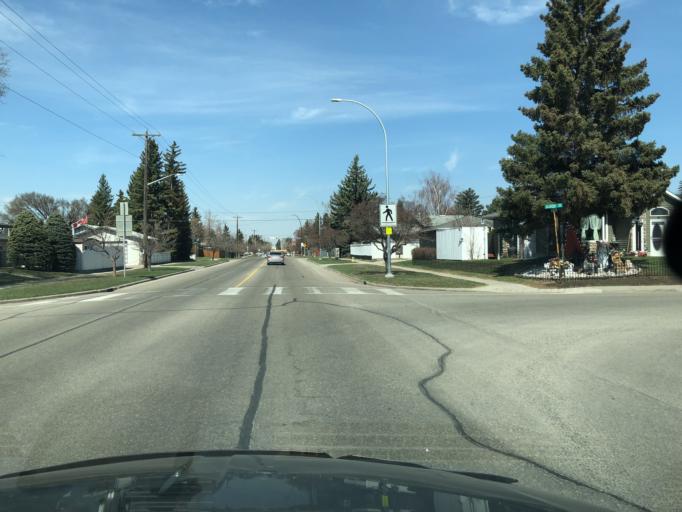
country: CA
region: Alberta
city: Calgary
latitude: 50.9666
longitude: -114.0485
